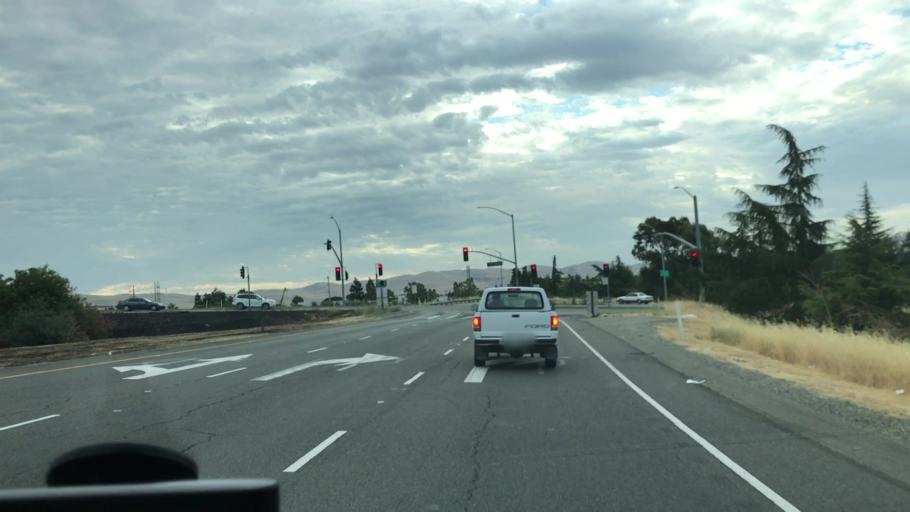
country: US
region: California
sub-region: Alameda County
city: Livermore
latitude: 37.7019
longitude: -121.7415
